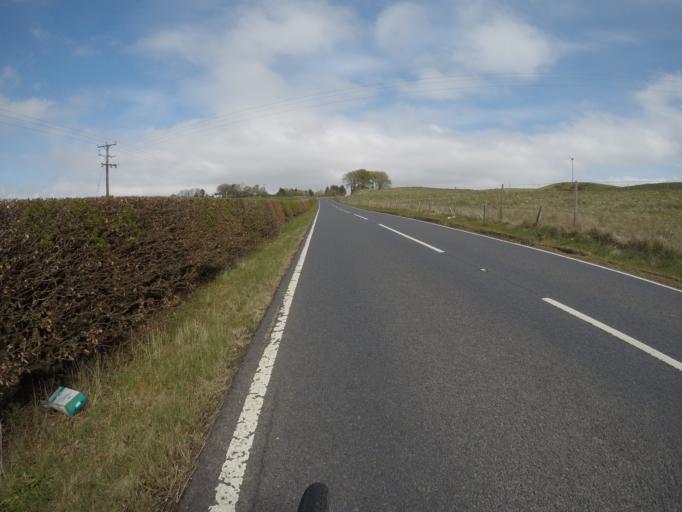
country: GB
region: Scotland
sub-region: East Renfrewshire
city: Neilston
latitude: 55.7239
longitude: -4.4279
